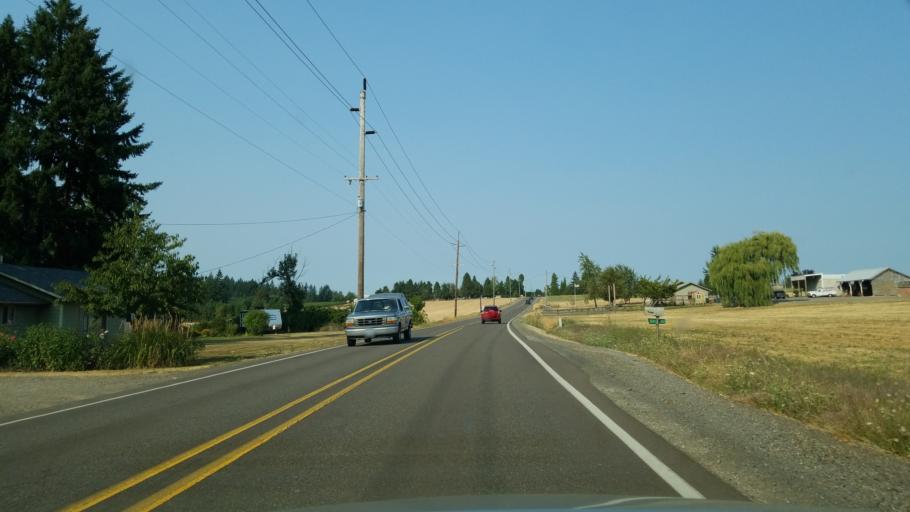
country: US
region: Oregon
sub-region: Clackamas County
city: Molalla
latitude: 45.0790
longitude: -122.6776
